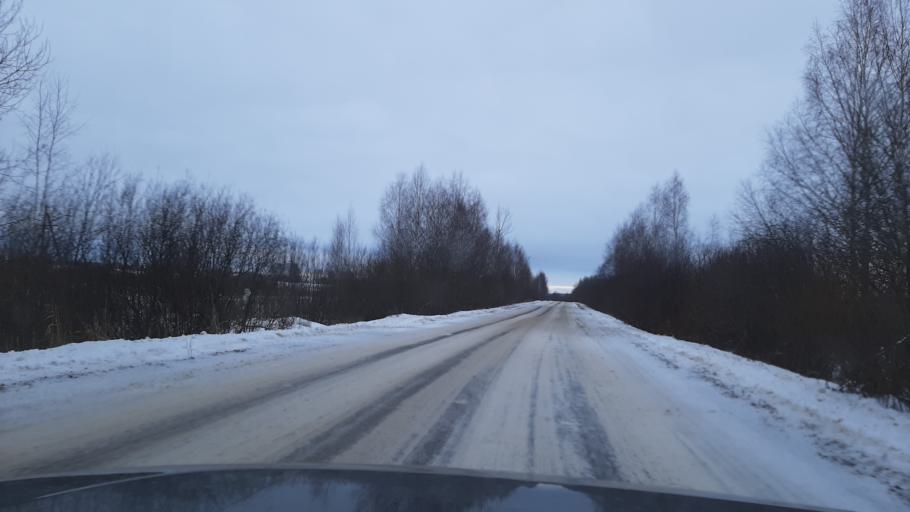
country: RU
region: Kostroma
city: Volgorechensk
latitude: 57.4398
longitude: 41.1077
